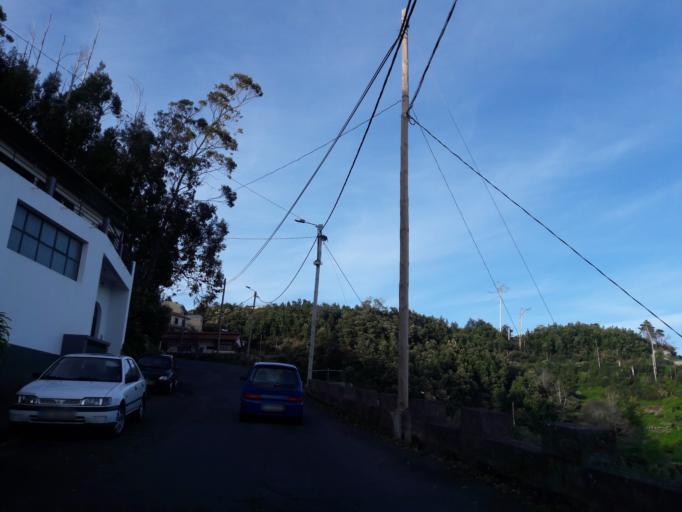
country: PT
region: Madeira
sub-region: Santa Cruz
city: Camacha
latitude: 32.6657
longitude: -16.8455
